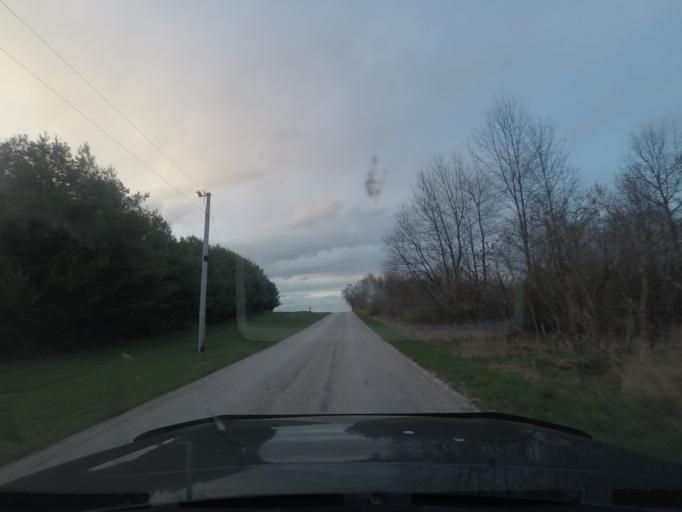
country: US
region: Indiana
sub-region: LaPorte County
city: Kingsford Heights
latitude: 41.4696
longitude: -86.7001
